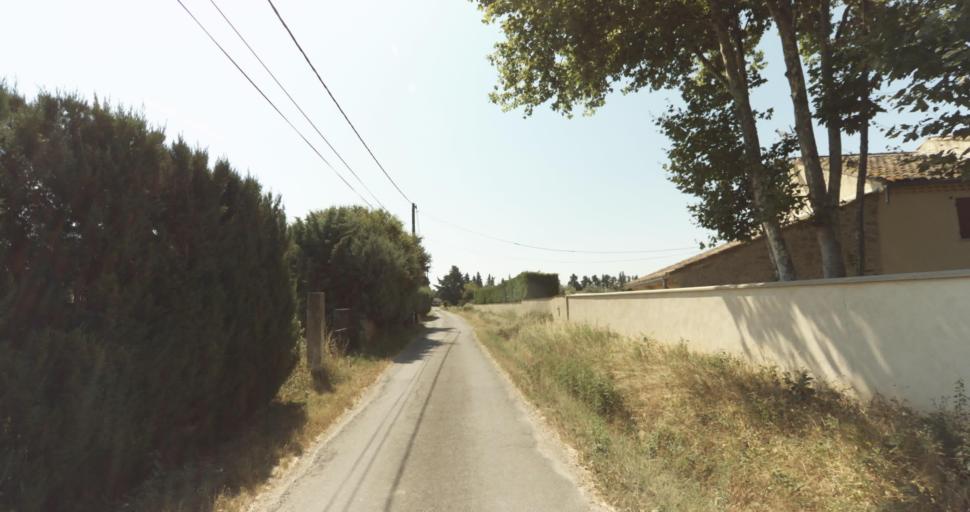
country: FR
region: Provence-Alpes-Cote d'Azur
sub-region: Departement du Vaucluse
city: Monteux
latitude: 44.0152
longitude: 5.0165
